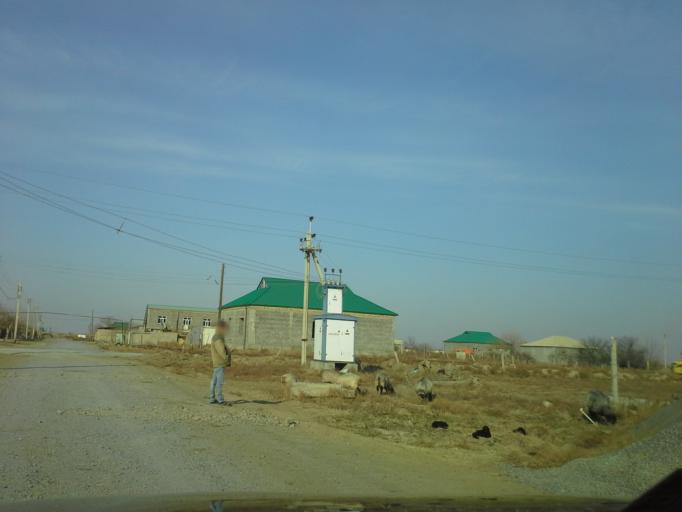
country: TM
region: Ahal
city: Abadan
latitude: 38.1779
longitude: 58.0473
